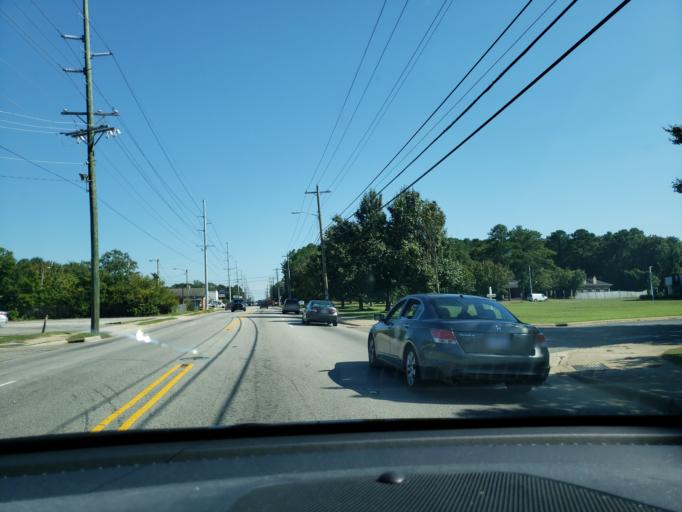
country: US
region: North Carolina
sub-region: Cumberland County
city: Fayetteville
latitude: 35.0894
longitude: -78.9091
